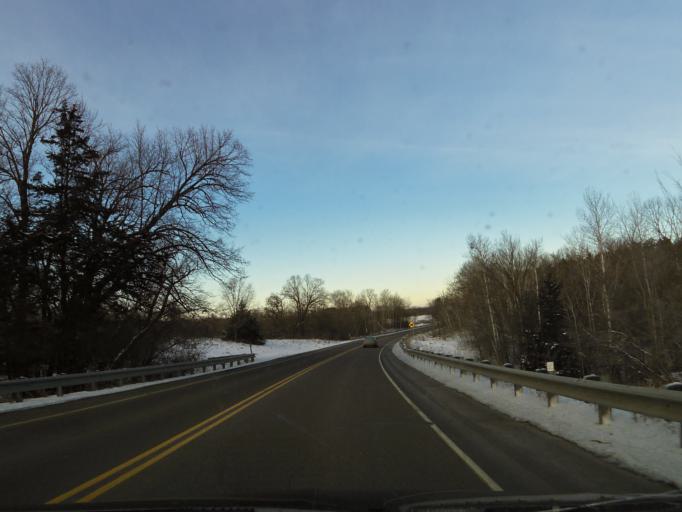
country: US
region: Wisconsin
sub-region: Polk County
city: Osceola
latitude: 45.3409
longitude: -92.7241
